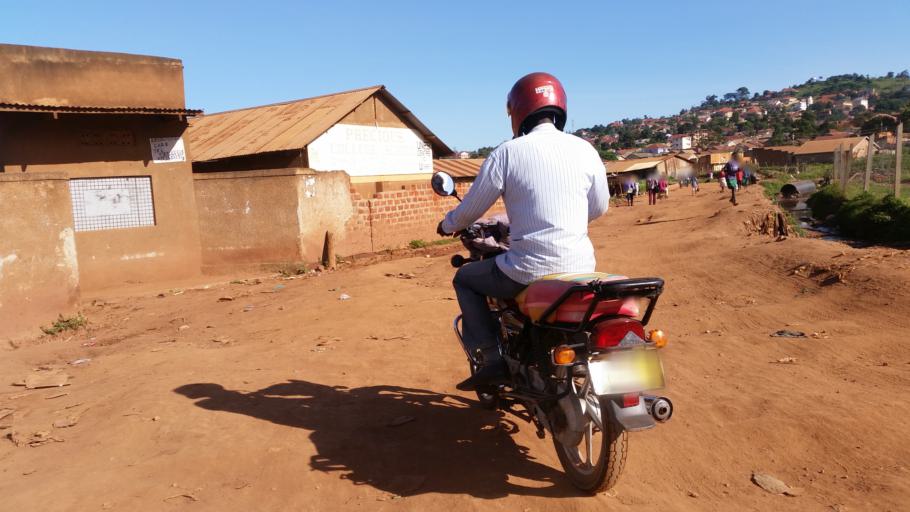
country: UG
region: Central Region
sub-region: Wakiso District
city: Kireka
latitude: 0.3270
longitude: 32.6466
